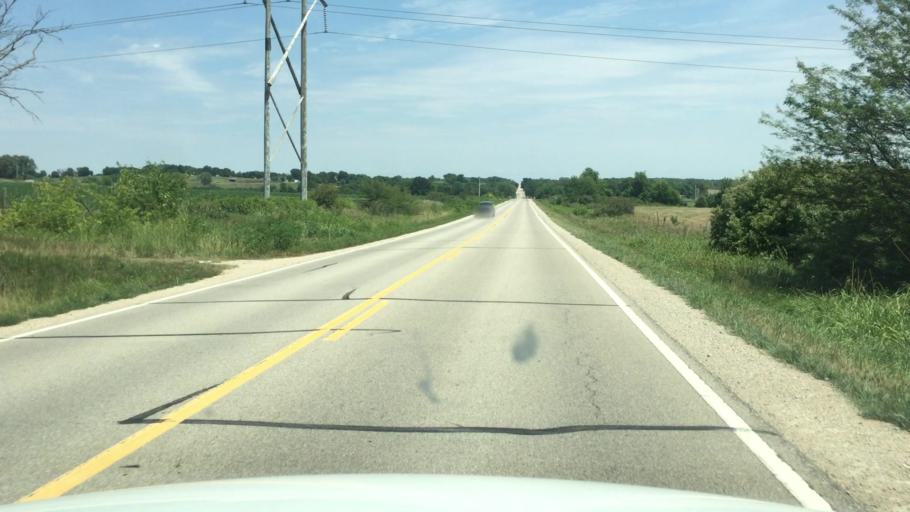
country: US
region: Kansas
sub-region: Osage County
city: Overbrook
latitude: 38.9712
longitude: -95.4713
